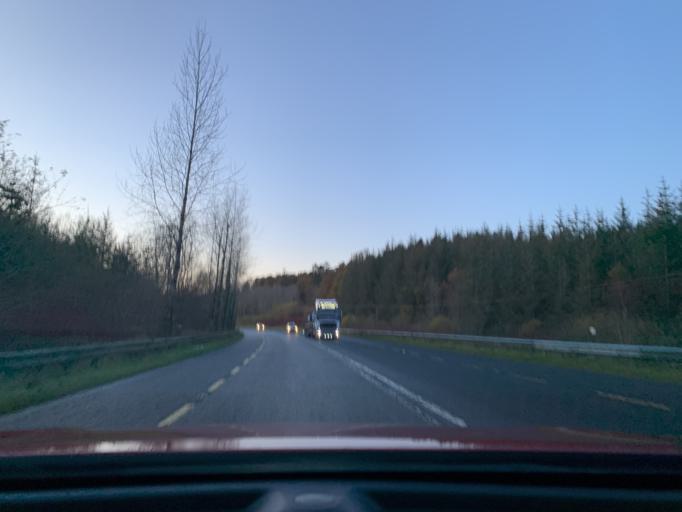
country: IE
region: Connaught
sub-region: County Leitrim
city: Carrick-on-Shannon
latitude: 53.9354
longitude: -8.0092
